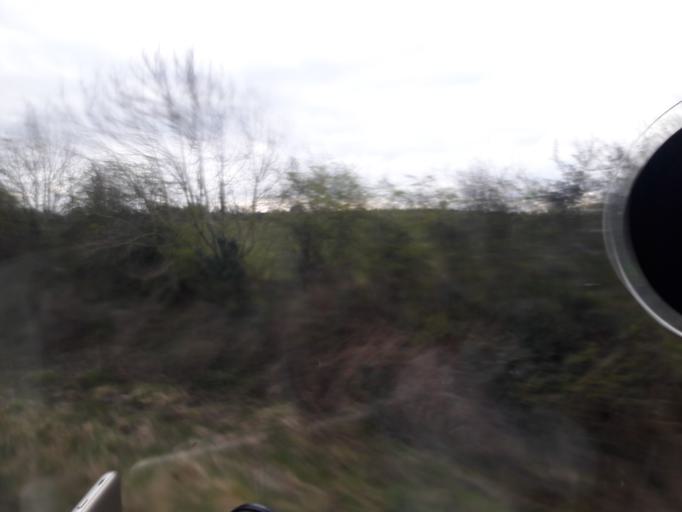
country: IE
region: Leinster
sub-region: An Longfort
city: Granard
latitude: 53.6743
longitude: -7.5241
